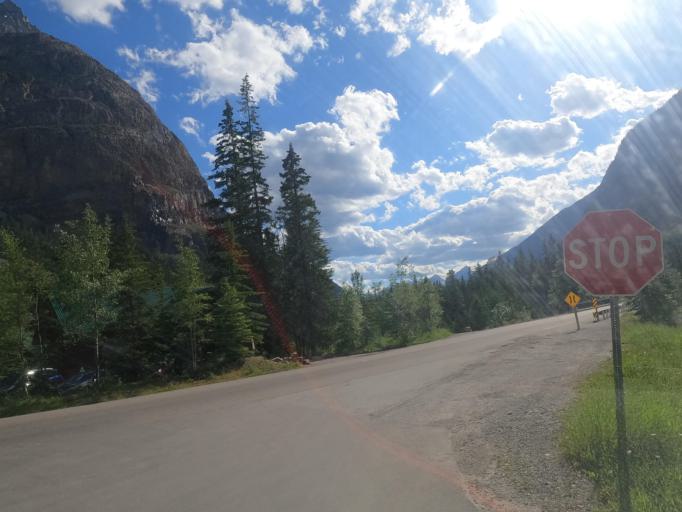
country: CA
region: Alberta
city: Lake Louise
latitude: 51.4230
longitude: -116.4354
